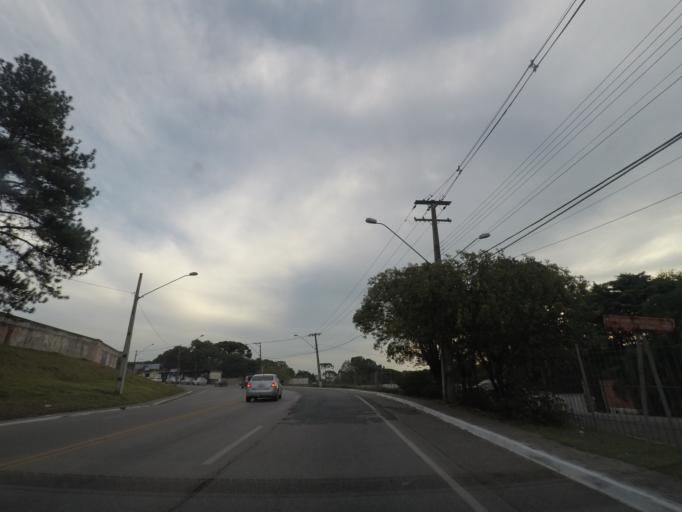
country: BR
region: Parana
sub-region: Curitiba
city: Curitiba
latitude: -25.3733
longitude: -49.2222
